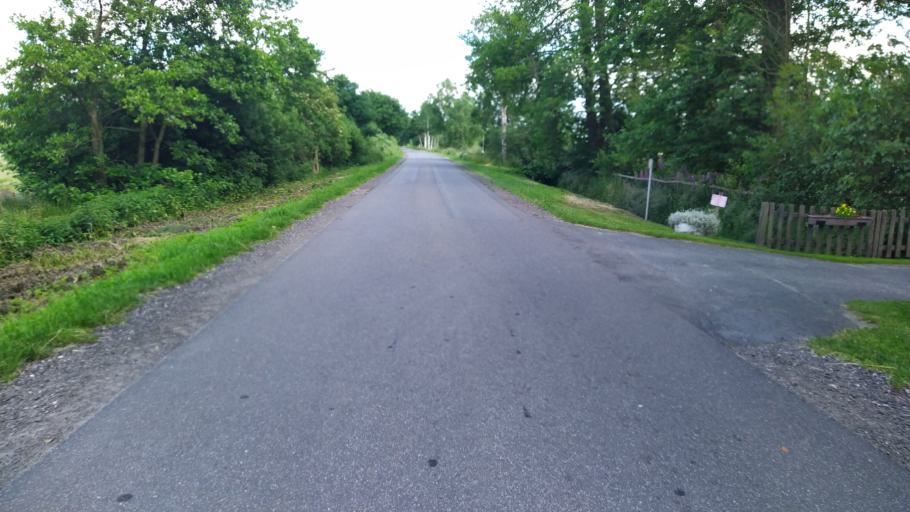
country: DE
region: Lower Saxony
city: Steinau
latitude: 53.6551
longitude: 8.9031
